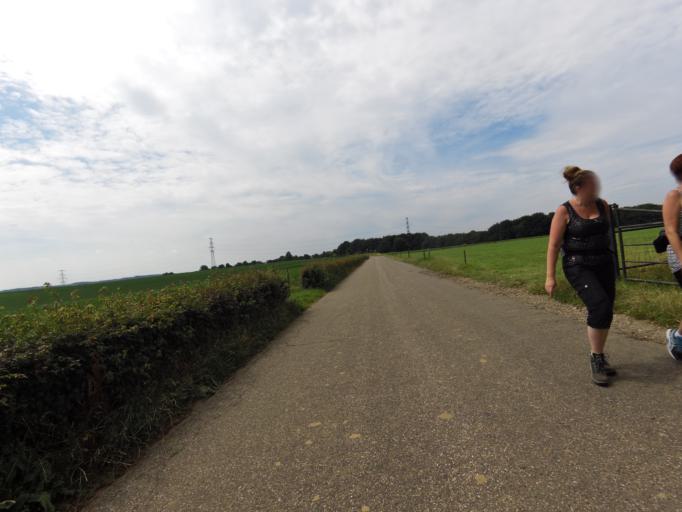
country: NL
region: Limburg
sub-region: Gemeente Voerendaal
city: Klimmen
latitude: 50.8726
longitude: 5.8738
